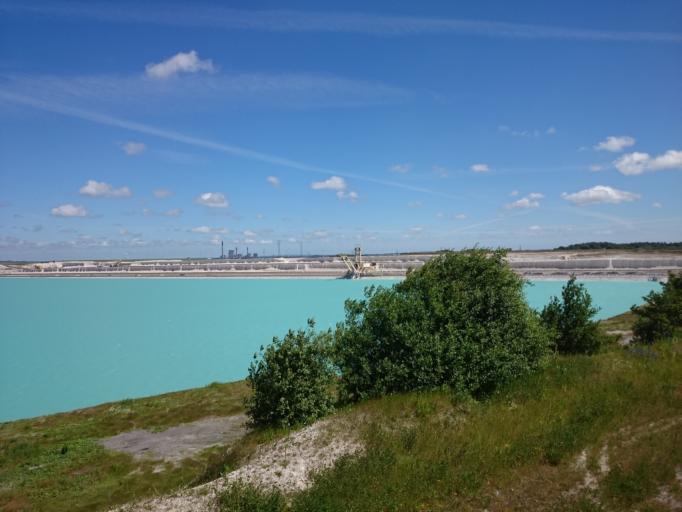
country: DK
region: North Denmark
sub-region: Alborg Kommune
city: Gistrup
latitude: 57.0419
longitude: 9.9887
